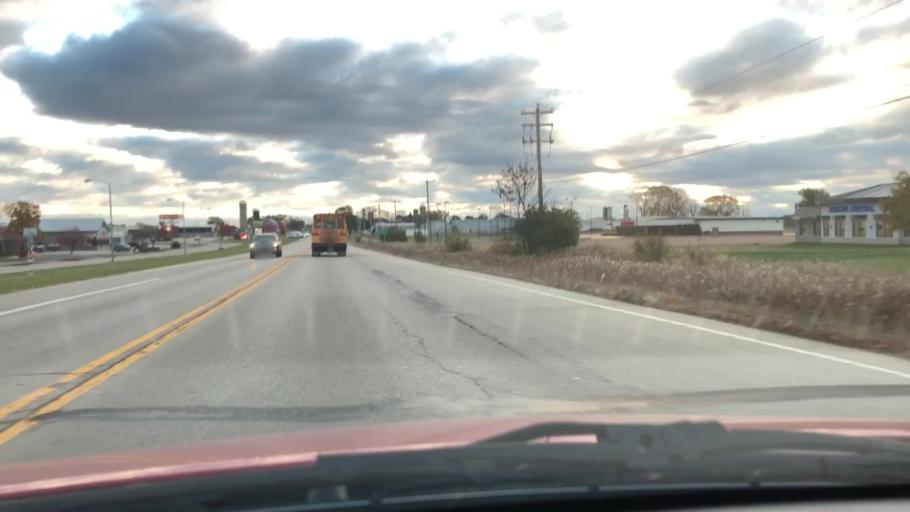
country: US
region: Wisconsin
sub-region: Outagamie County
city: Seymour
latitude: 44.5004
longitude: -88.3247
